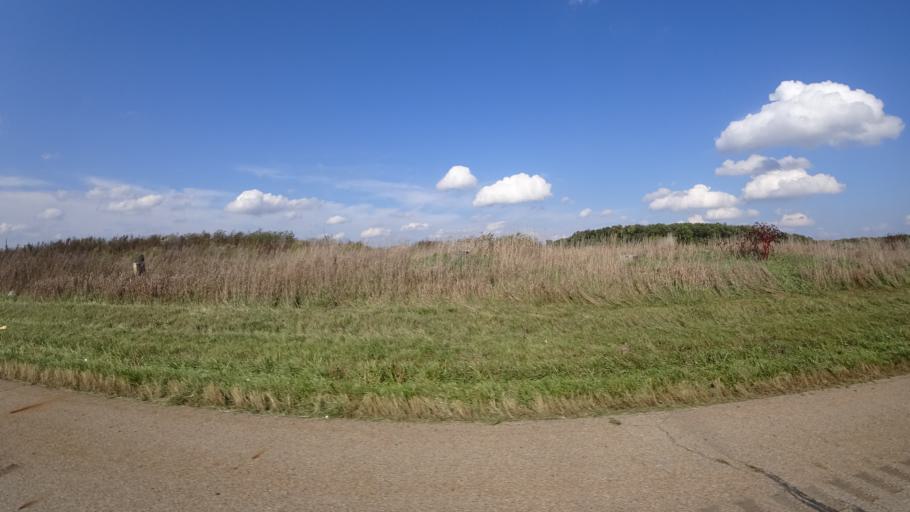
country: US
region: Michigan
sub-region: Calhoun County
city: Homer
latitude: 42.1618
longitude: -84.7376
